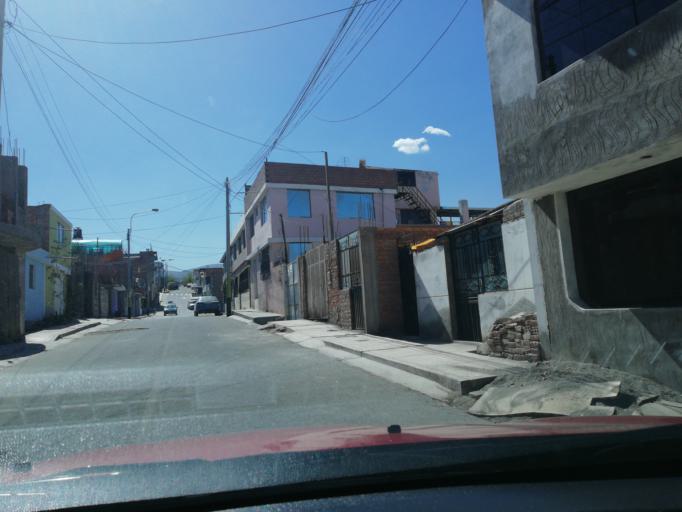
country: PE
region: Arequipa
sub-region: Provincia de Arequipa
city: Arequipa
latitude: -16.3696
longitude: -71.5264
